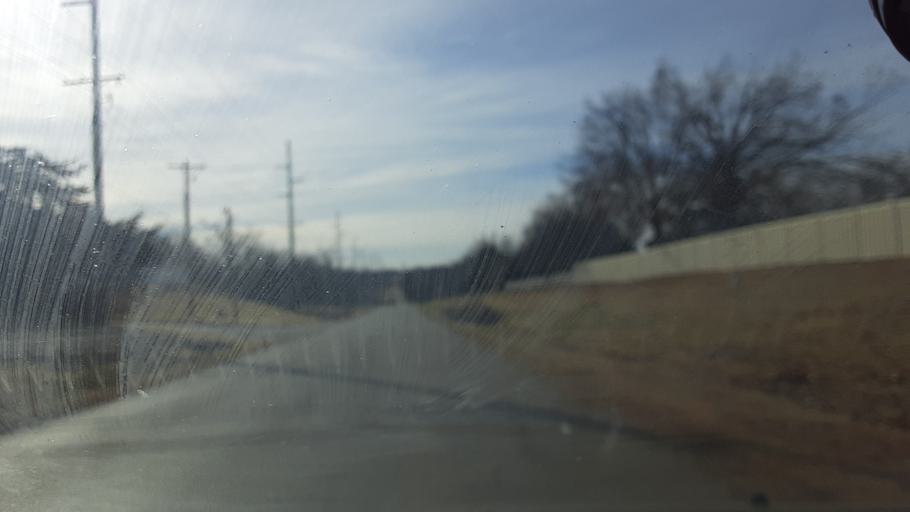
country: US
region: Oklahoma
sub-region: Logan County
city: Guthrie
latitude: 35.8910
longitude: -97.4075
